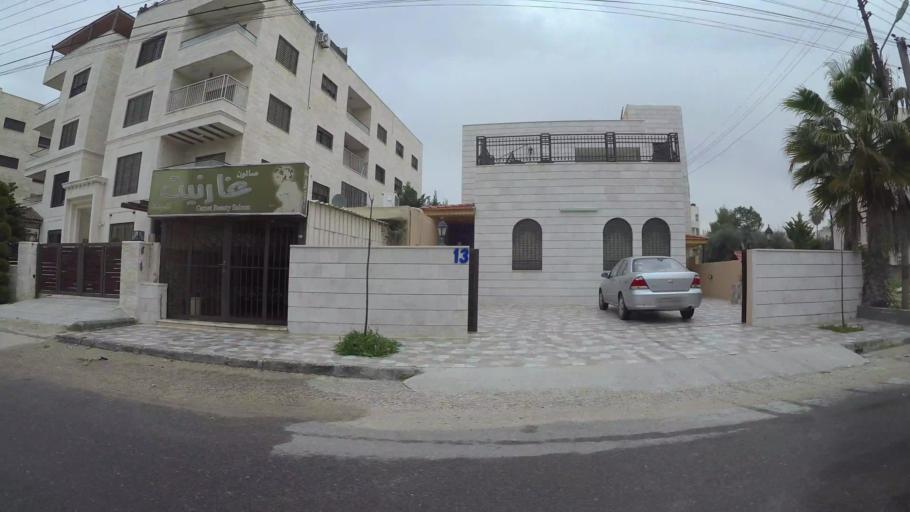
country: JO
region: Amman
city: Umm as Summaq
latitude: 31.8913
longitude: 35.8552
